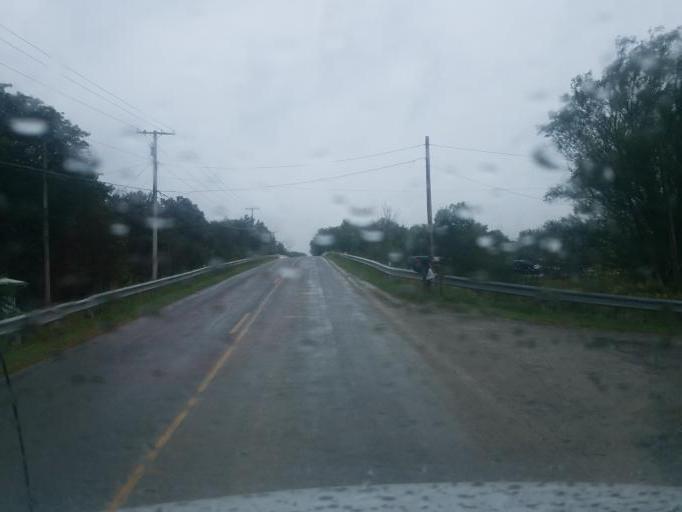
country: US
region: Ohio
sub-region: Medina County
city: Seville
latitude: 41.0335
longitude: -81.8324
